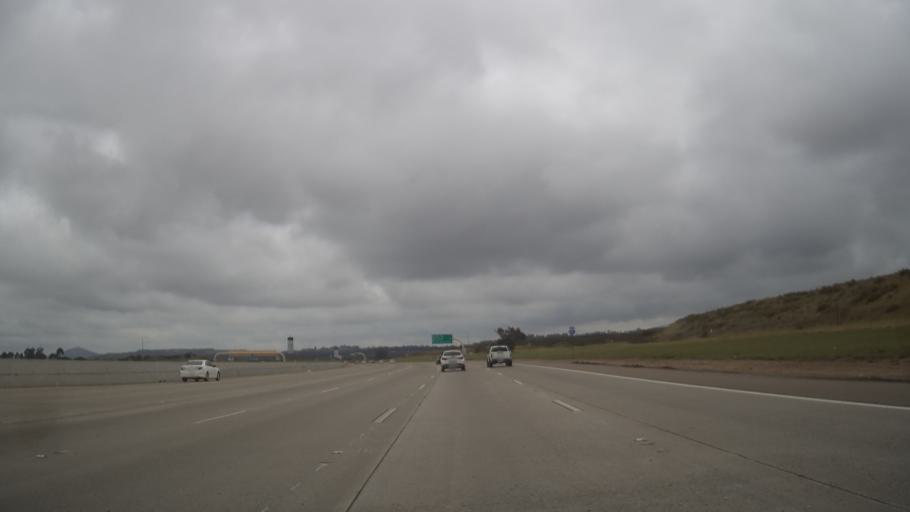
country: US
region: California
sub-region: San Diego County
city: Poway
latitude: 32.8659
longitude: -117.1079
